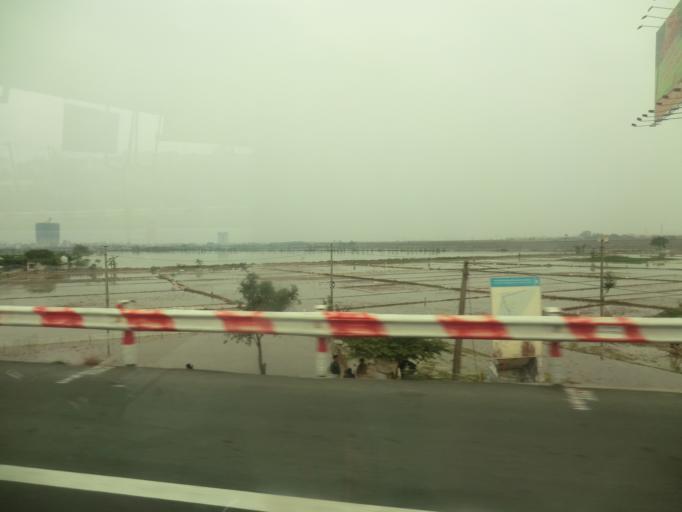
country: VN
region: Ha Noi
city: Van Dien
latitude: 20.9454
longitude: 105.8581
